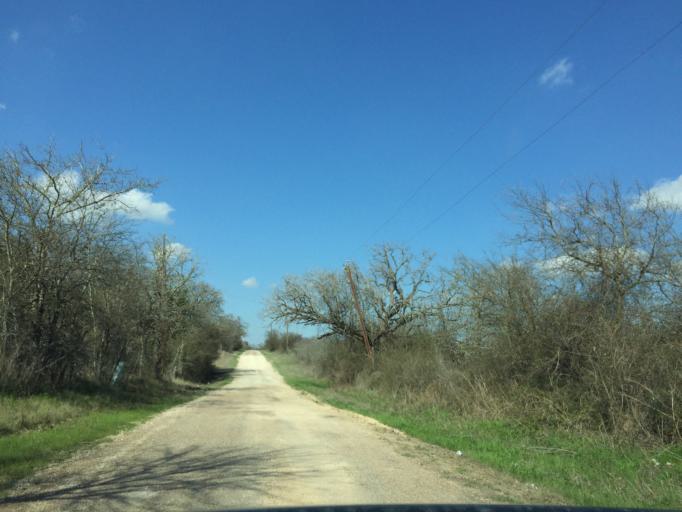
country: US
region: Texas
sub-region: Milam County
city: Thorndale
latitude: 30.5557
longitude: -97.1454
